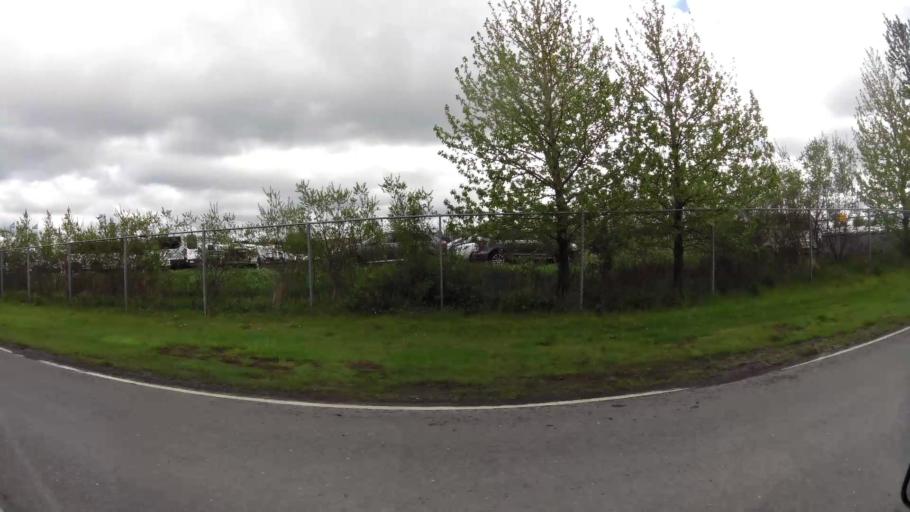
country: IS
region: Capital Region
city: Kopavogur
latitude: 64.1337
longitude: -21.9479
